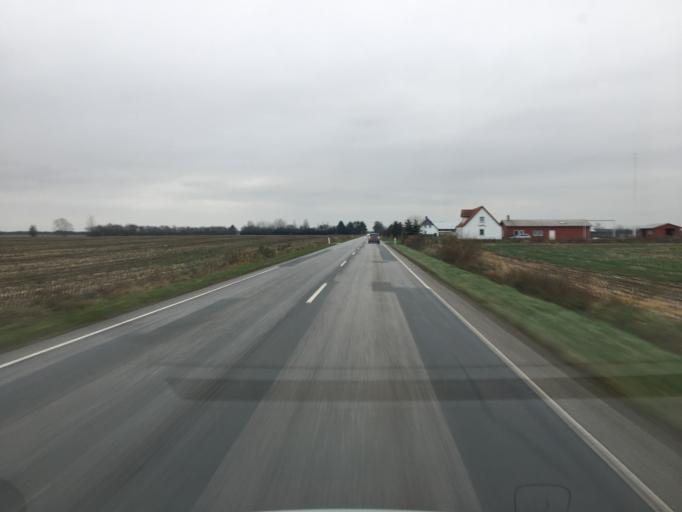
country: DK
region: South Denmark
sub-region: Aabenraa Kommune
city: Tinglev
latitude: 54.9901
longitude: 9.1846
